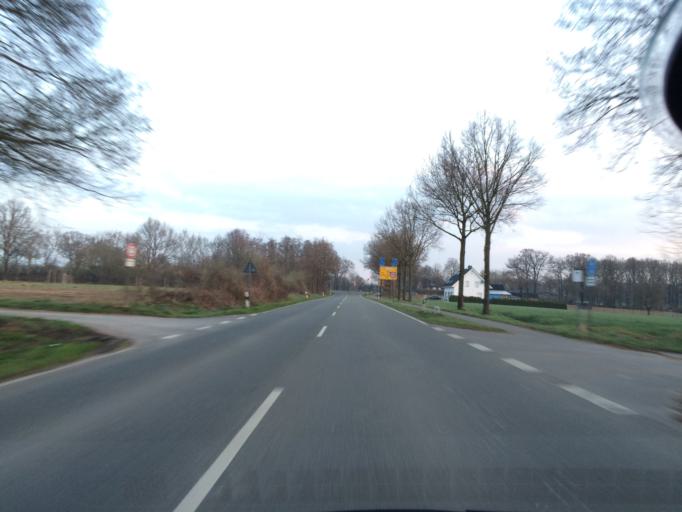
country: DE
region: North Rhine-Westphalia
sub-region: Regierungsbezirk Munster
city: Haltern
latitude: 51.7250
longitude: 7.1226
